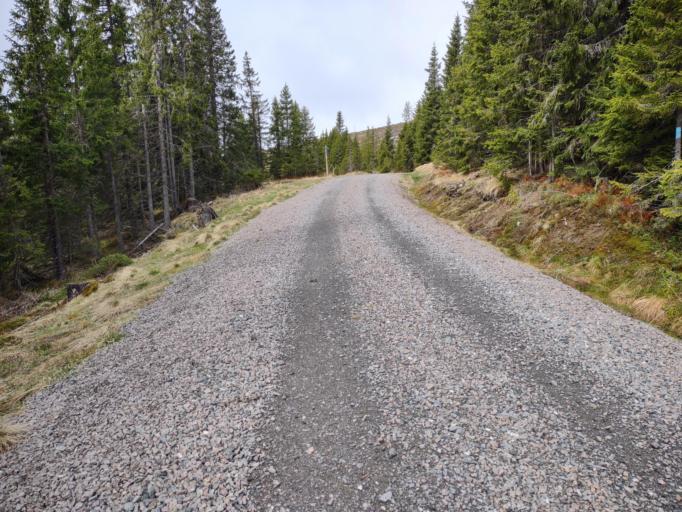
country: NO
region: Oppland
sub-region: Gran
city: Jaren
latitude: 60.4205
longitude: 10.6877
